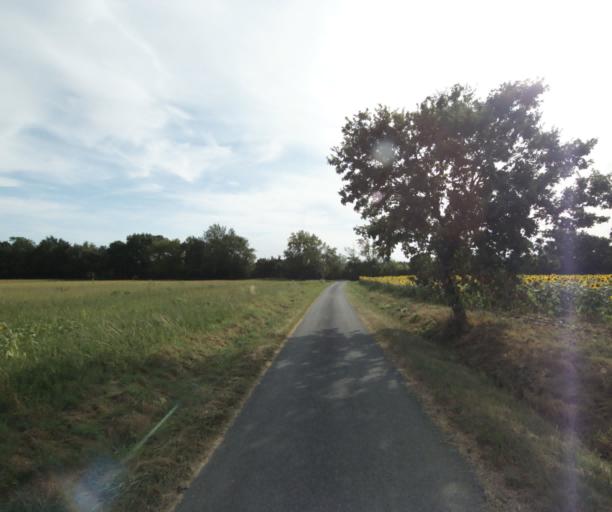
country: FR
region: Midi-Pyrenees
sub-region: Departement du Tarn
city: Puylaurens
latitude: 43.5295
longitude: 2.0457
